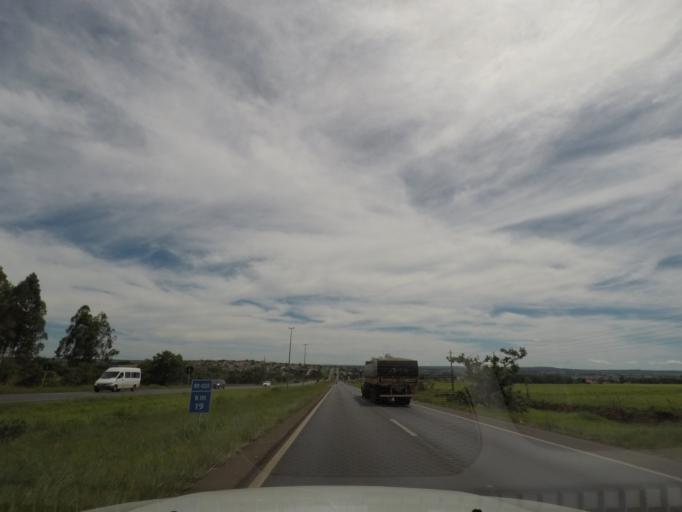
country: BR
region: Goias
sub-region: Planaltina
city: Planaltina
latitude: -15.6125
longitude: -47.7011
